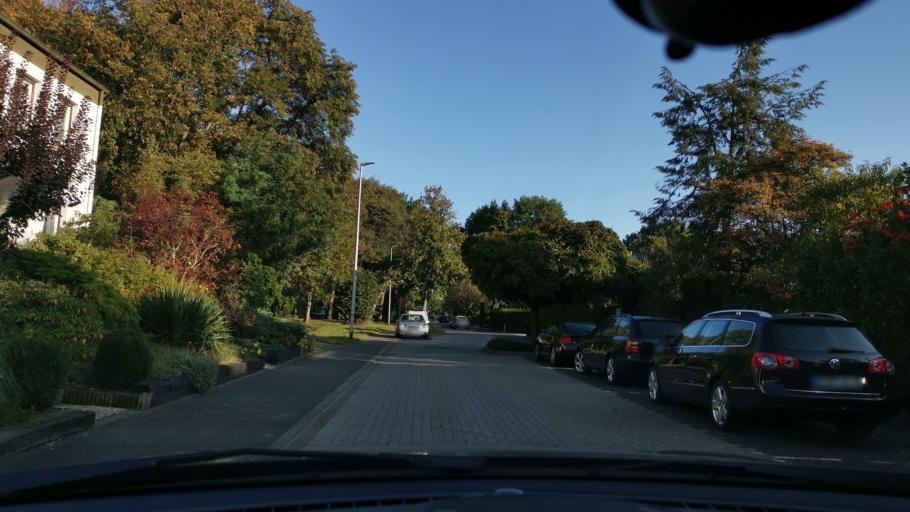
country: DE
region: North Rhine-Westphalia
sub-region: Regierungsbezirk Dusseldorf
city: Rommerskirchen
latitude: 51.1032
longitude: 6.7211
